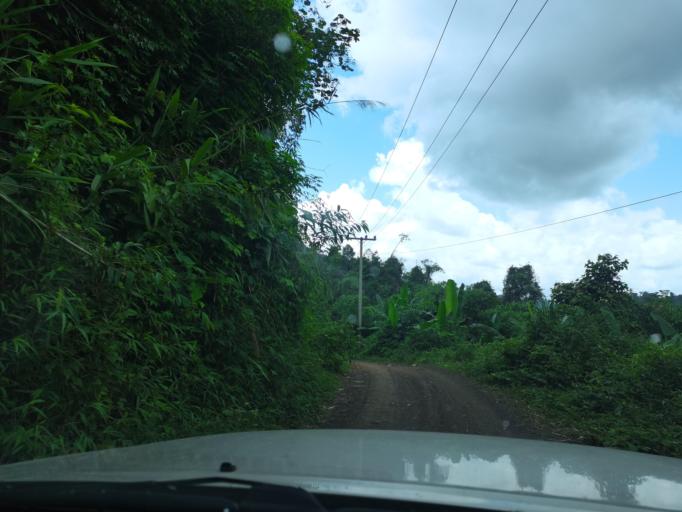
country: LA
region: Loungnamtha
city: Muang Long
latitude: 20.7679
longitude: 101.0175
